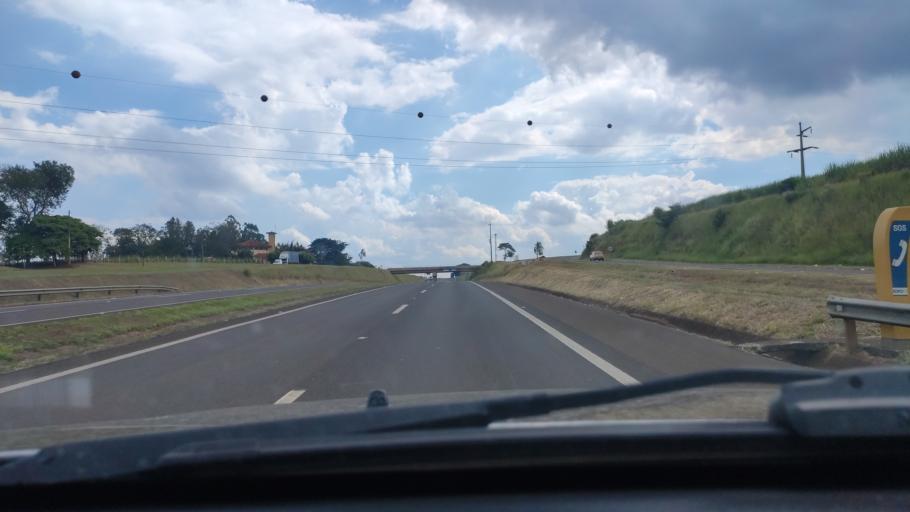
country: BR
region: Sao Paulo
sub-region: Itapui
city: Itapui
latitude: -22.3091
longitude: -48.6889
